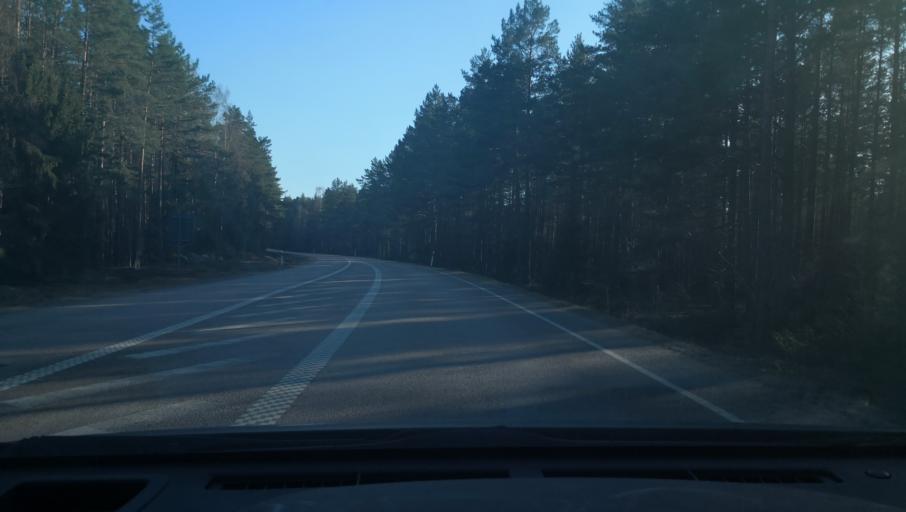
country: SE
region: Uppsala
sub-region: Heby Kommun
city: Heby
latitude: 60.0110
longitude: 16.8393
